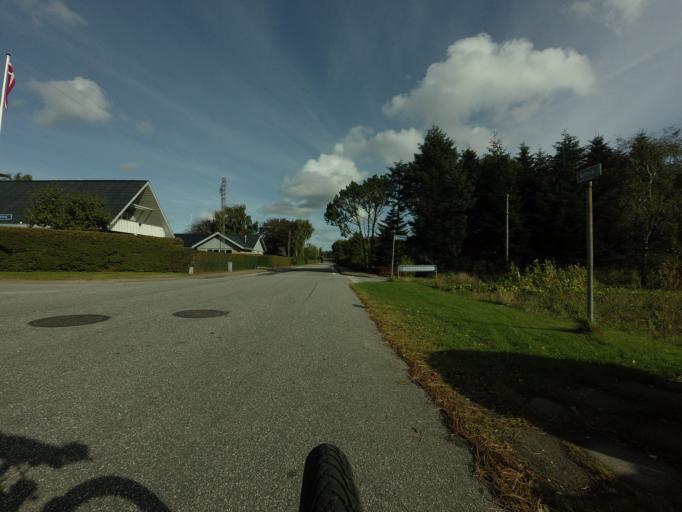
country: DK
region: Central Jutland
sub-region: Viborg Kommune
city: Bjerringbro
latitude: 56.4771
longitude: 9.6208
